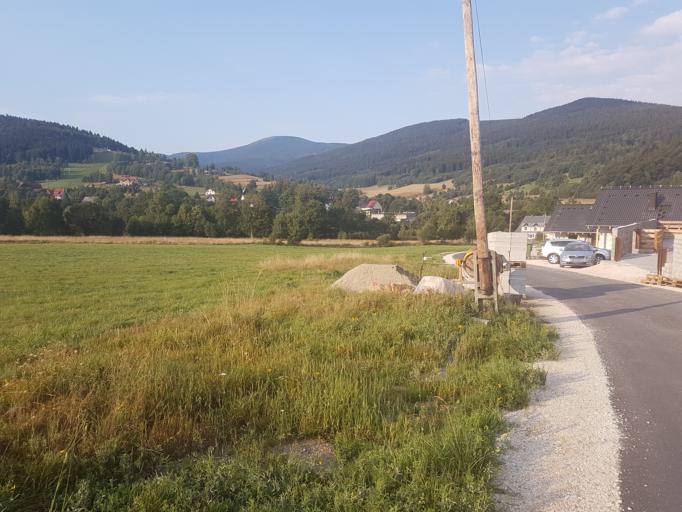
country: PL
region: Lower Silesian Voivodeship
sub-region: Powiat klodzki
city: Stronie Slaskie
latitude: 50.2611
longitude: 16.8958
